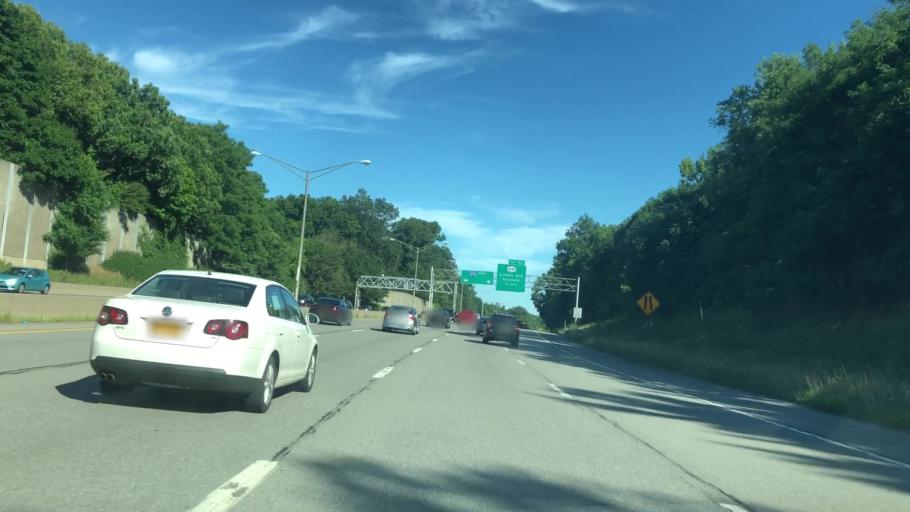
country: US
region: New York
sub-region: Monroe County
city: Brighton
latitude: 43.1370
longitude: -77.5348
